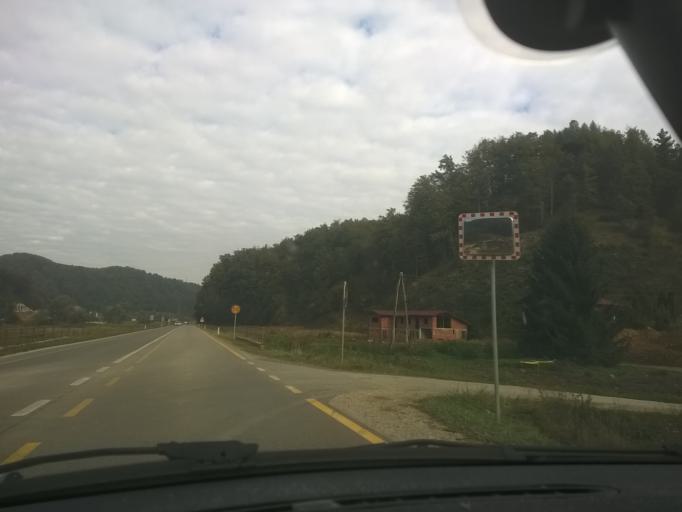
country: SI
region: Zetale
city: Zetale
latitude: 46.2933
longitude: 15.8560
